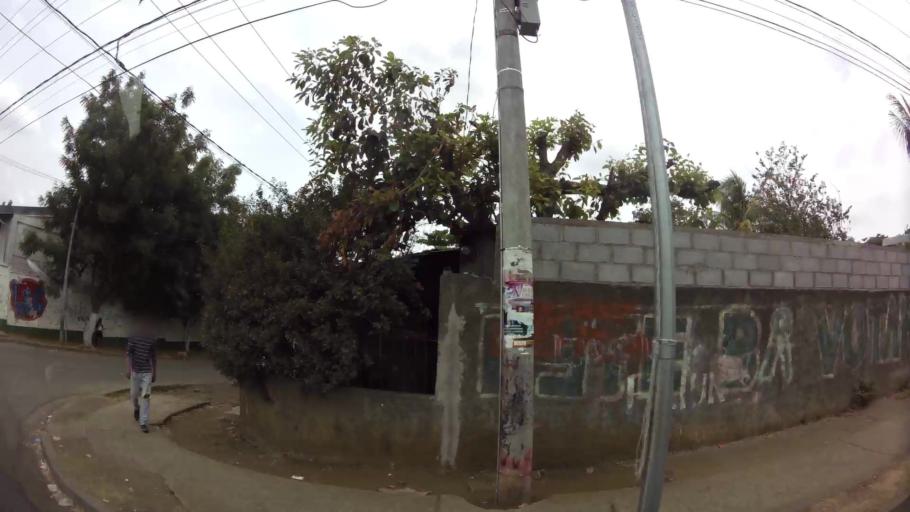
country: NI
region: Managua
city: Managua
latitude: 12.1094
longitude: -86.2246
